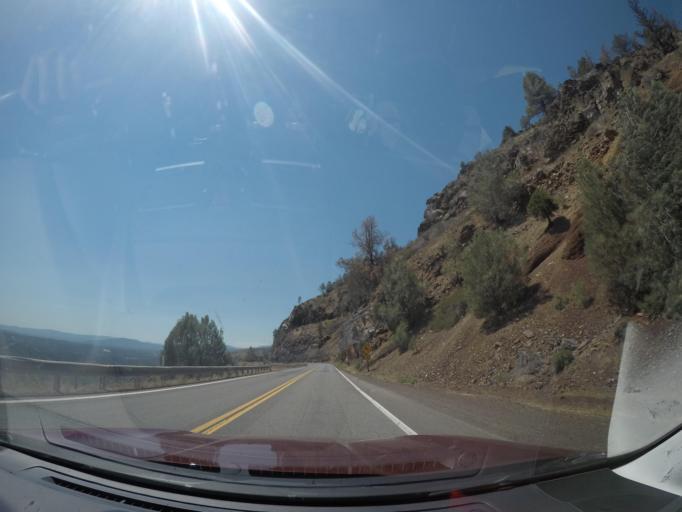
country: US
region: California
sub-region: Shasta County
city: Burney
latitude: 40.9930
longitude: -121.4846
